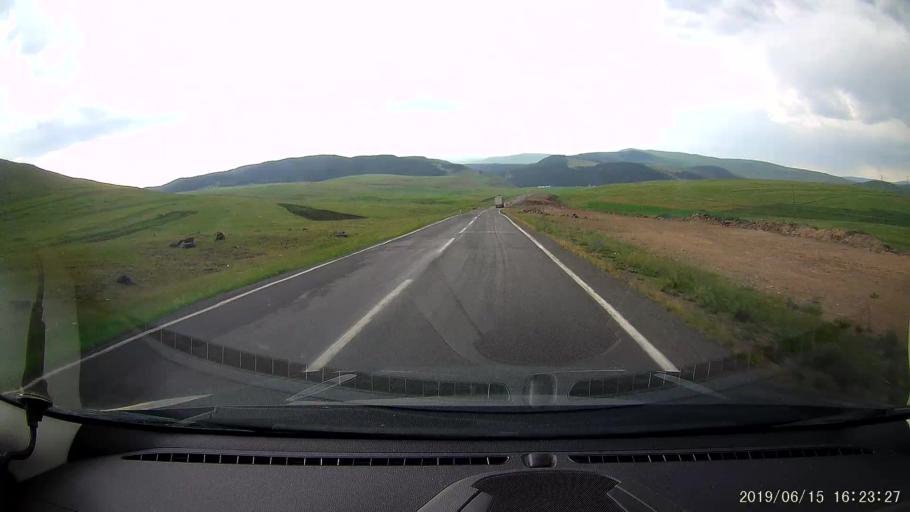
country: TR
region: Ardahan
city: Hanak
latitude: 41.1779
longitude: 42.8627
